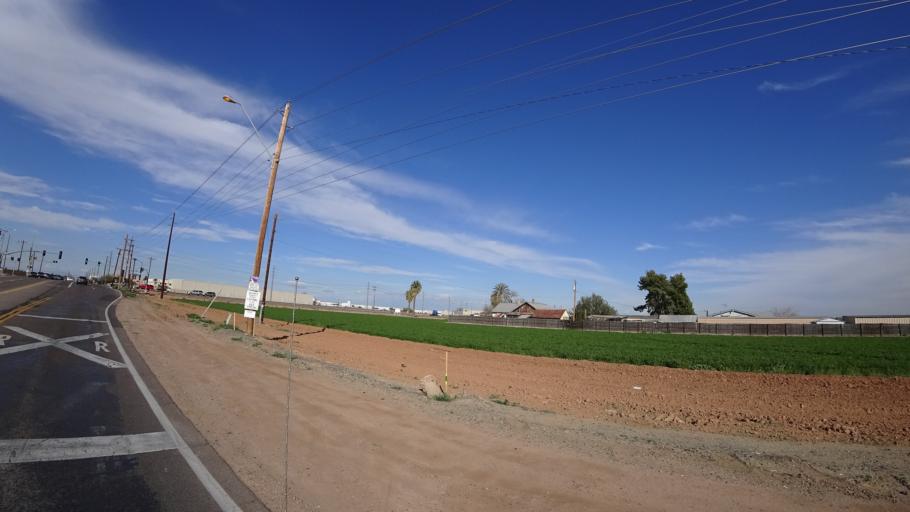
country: US
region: Arizona
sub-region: Maricopa County
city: Tolleson
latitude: 33.4342
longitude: -112.2897
